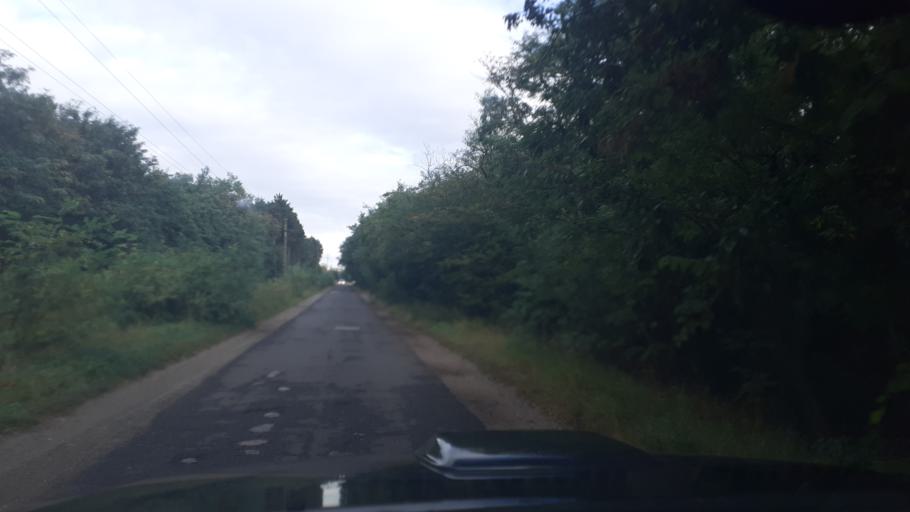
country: HU
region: Fejer
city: dunaujvaros
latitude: 46.9467
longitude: 18.8611
